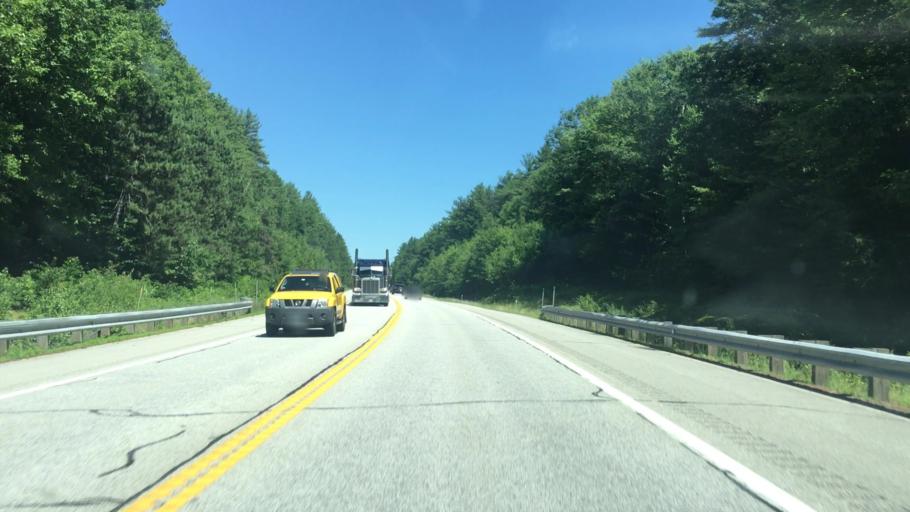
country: US
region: New Hampshire
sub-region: Merrimack County
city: Contoocook
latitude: 43.1766
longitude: -71.7238
